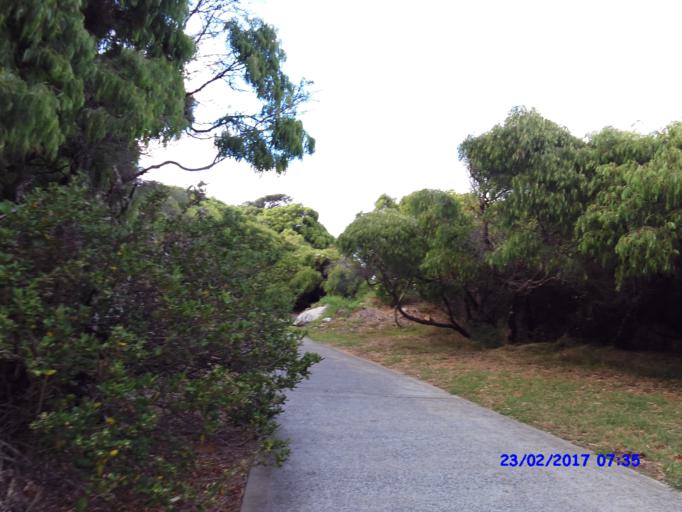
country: AU
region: Western Australia
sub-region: Augusta-Margaret River Shire
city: Augusta
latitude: -34.3256
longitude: 115.1702
